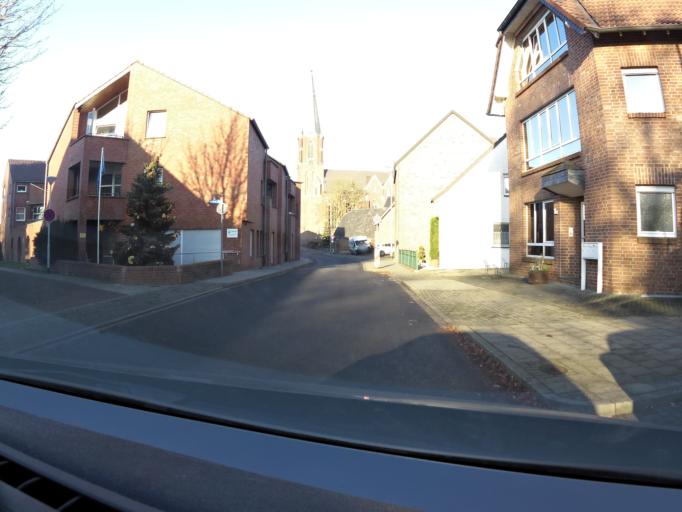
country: DE
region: North Rhine-Westphalia
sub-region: Regierungsbezirk Dusseldorf
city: Nettetal
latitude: 51.2796
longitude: 6.2422
